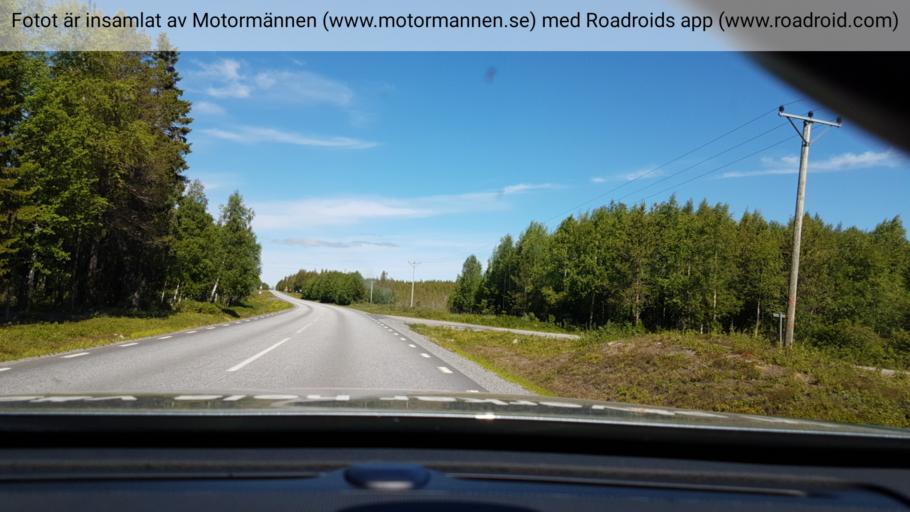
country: SE
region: Vaesterbotten
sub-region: Vilhelmina Kommun
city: Vilhelmina
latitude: 64.5221
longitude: 16.7650
